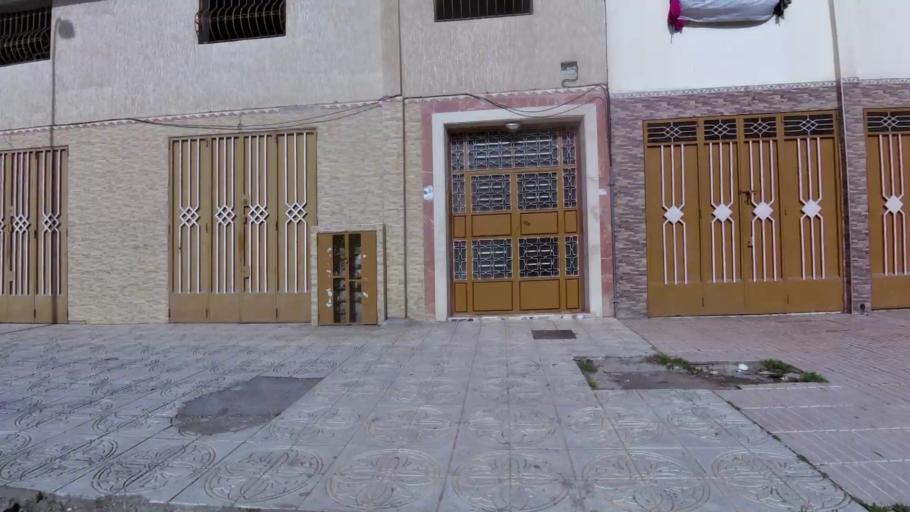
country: MA
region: Tanger-Tetouan
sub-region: Tanger-Assilah
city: Tangier
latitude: 35.7373
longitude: -5.8007
